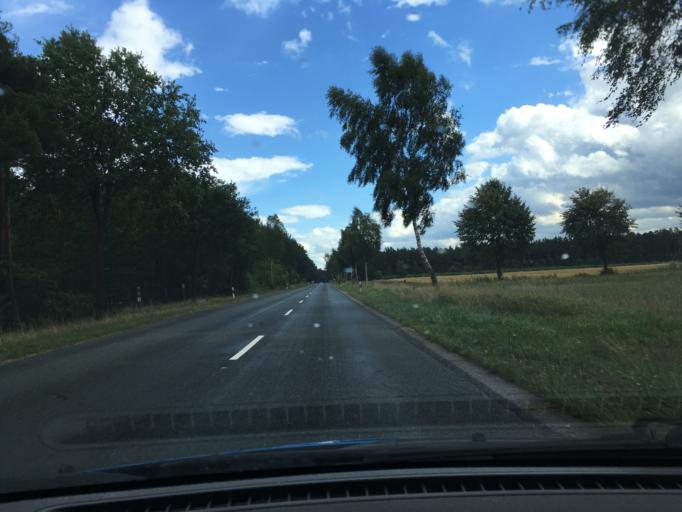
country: DE
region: Lower Saxony
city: Wietzendorf
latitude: 52.9248
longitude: 10.0076
